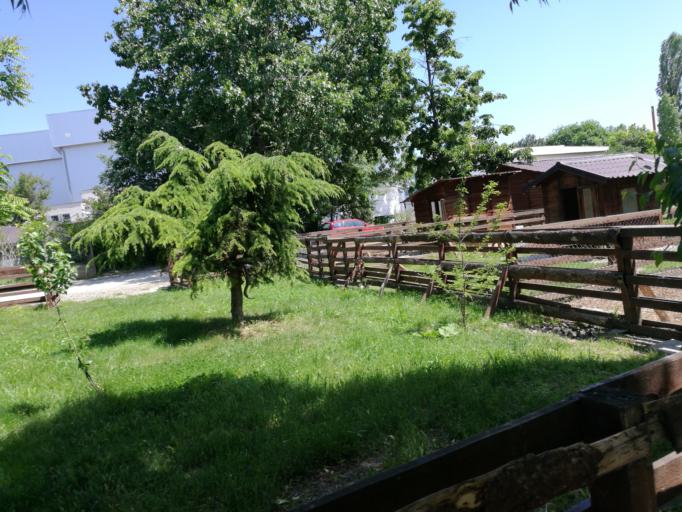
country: RO
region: Constanta
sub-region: Municipiul Constanta
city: Constanta
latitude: 44.2057
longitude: 28.6420
